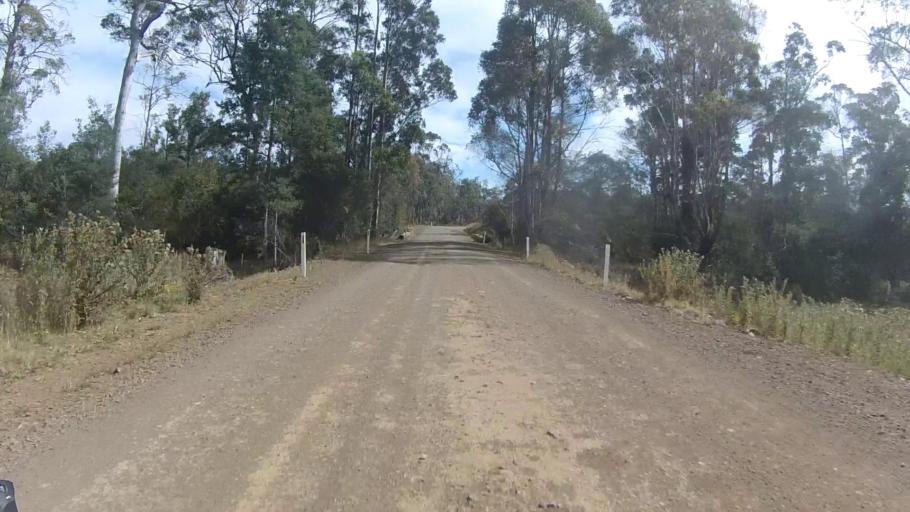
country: AU
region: Tasmania
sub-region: Sorell
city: Sorell
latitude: -42.6516
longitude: 147.8981
